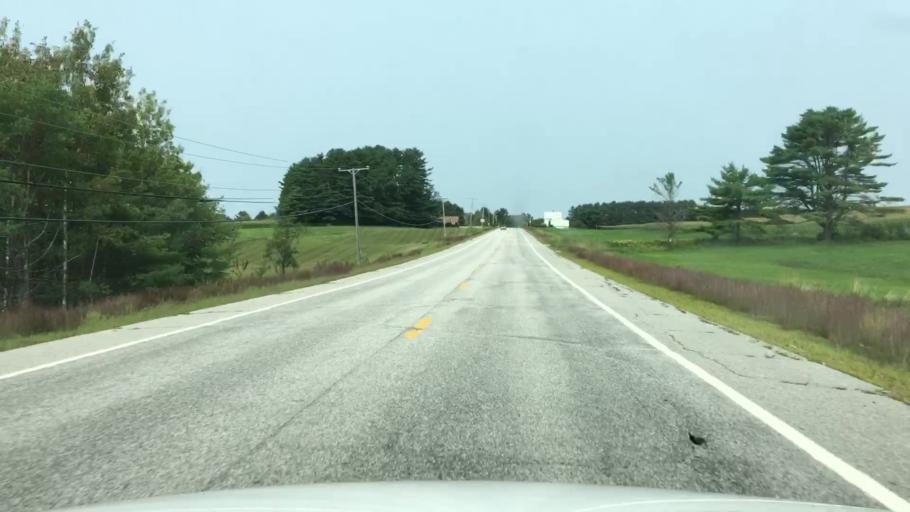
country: US
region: Maine
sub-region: Androscoggin County
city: Livermore Falls
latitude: 44.4085
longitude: -70.1372
